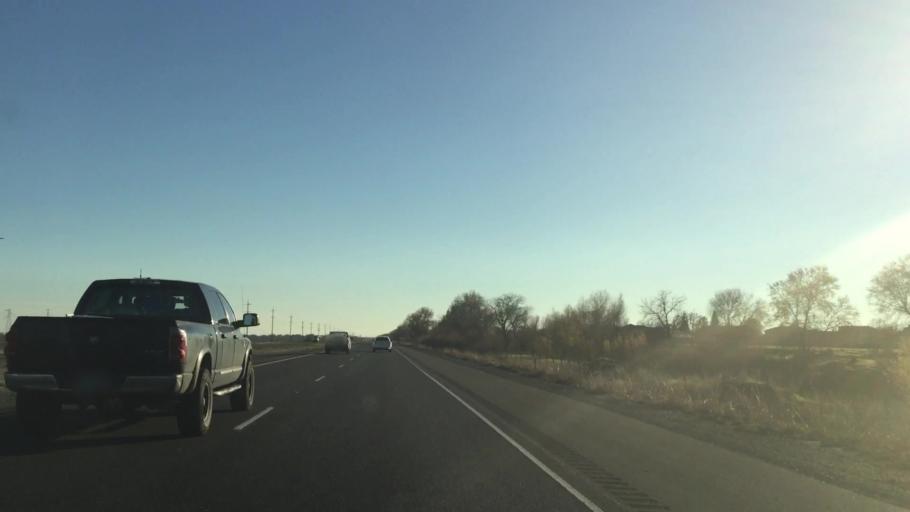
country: US
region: California
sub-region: Yuba County
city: Plumas Lake
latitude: 39.0062
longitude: -121.5434
